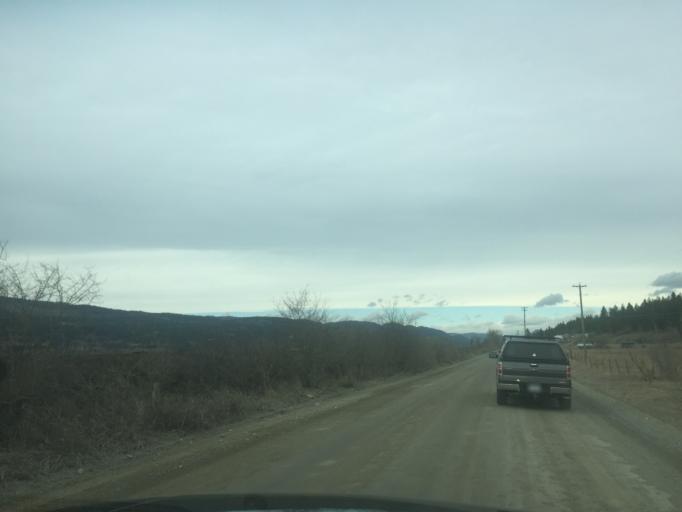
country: CA
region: British Columbia
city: Kamloops
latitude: 51.2495
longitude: -120.1500
